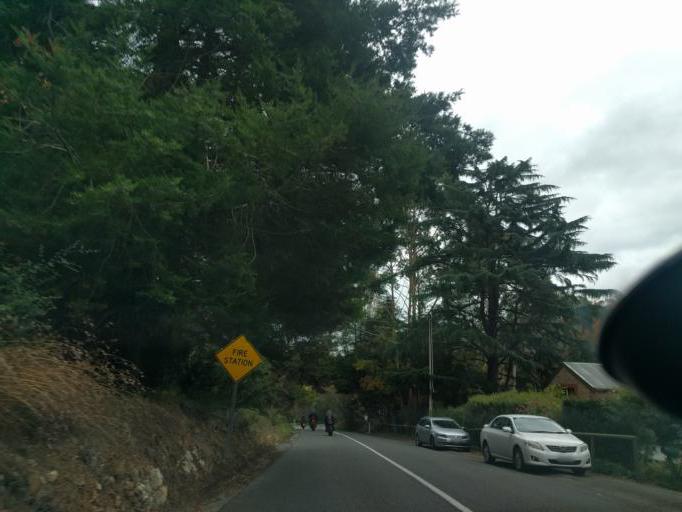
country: AU
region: South Australia
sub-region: Adelaide Hills
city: Stirling
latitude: -35.0165
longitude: 138.7402
